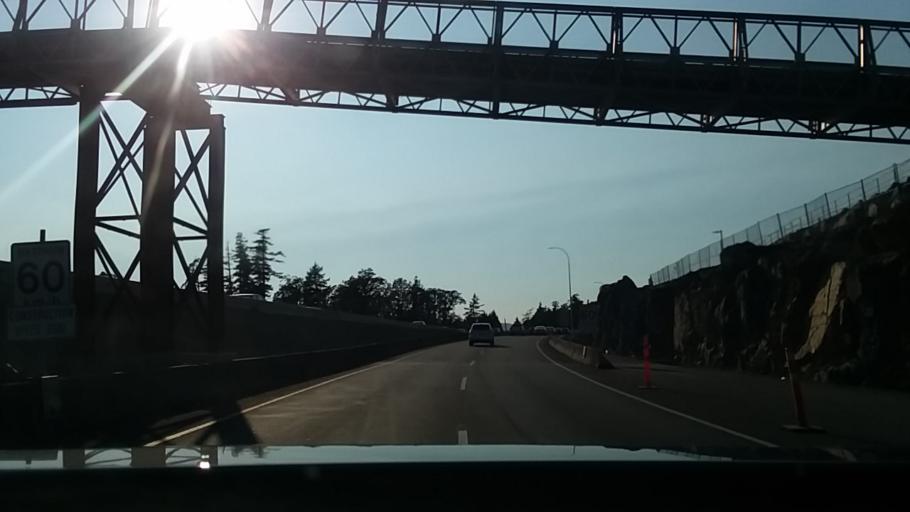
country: CA
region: British Columbia
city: Victoria
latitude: 48.4607
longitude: -123.4077
